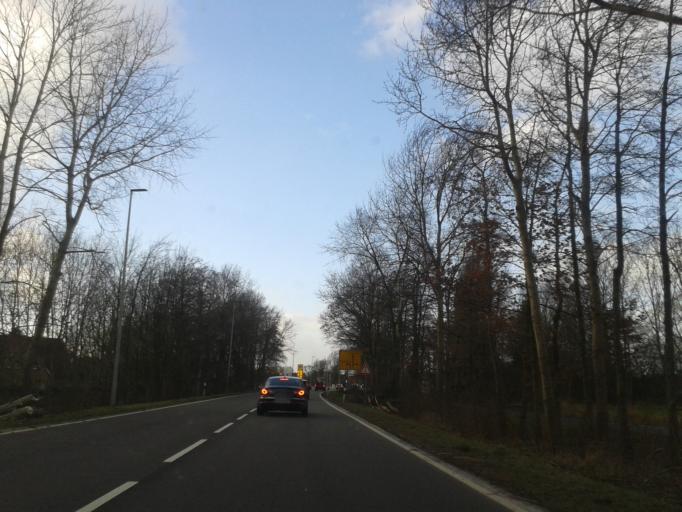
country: DE
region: Lower Saxony
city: Marienhafe
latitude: 53.5278
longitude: 7.2736
